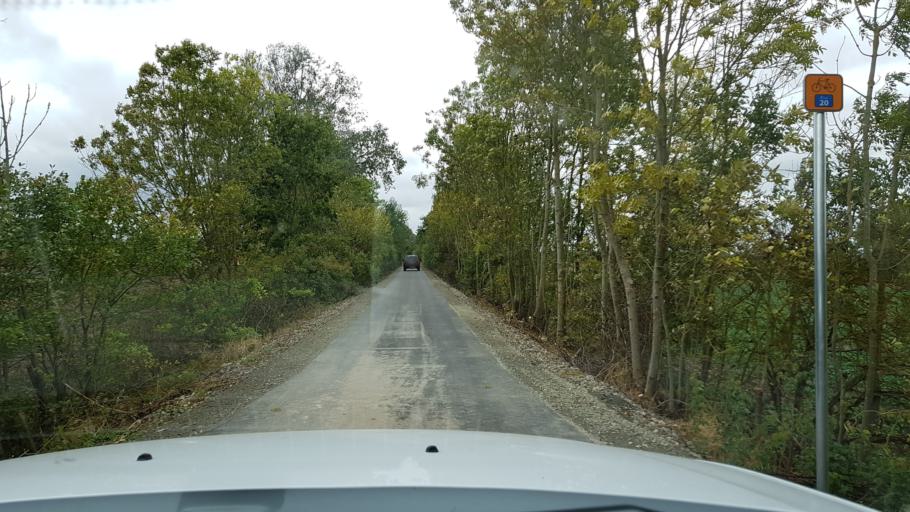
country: PL
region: West Pomeranian Voivodeship
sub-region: Powiat gryfinski
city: Moryn
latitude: 52.8651
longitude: 14.3427
